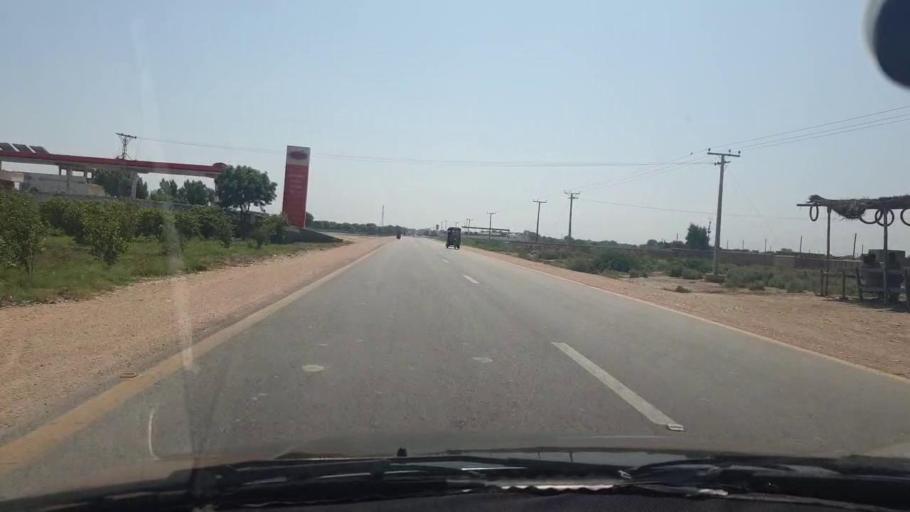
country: PK
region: Sindh
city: Chambar
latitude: 25.3128
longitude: 68.8056
